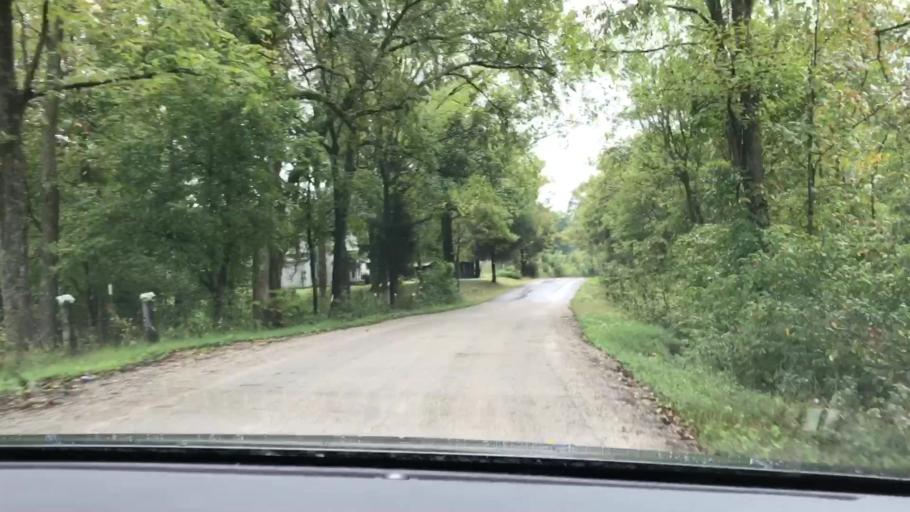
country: US
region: Tennessee
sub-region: Macon County
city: Red Boiling Springs
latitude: 36.5890
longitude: -85.7772
